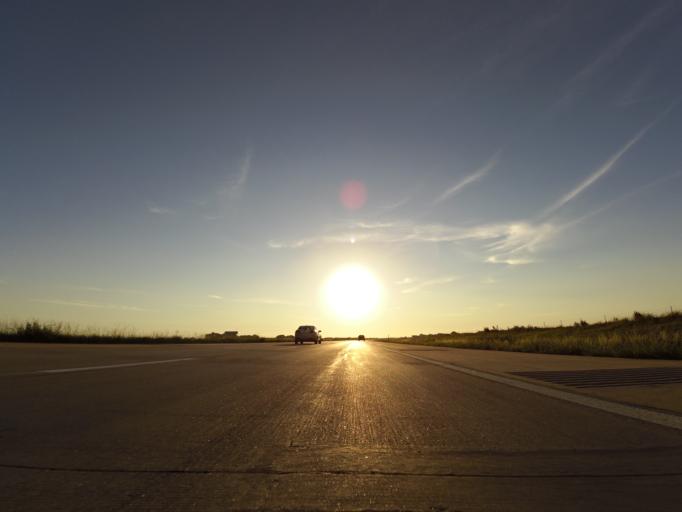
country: US
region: Kansas
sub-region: Reno County
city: Haven
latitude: 37.8755
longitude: -97.6829
